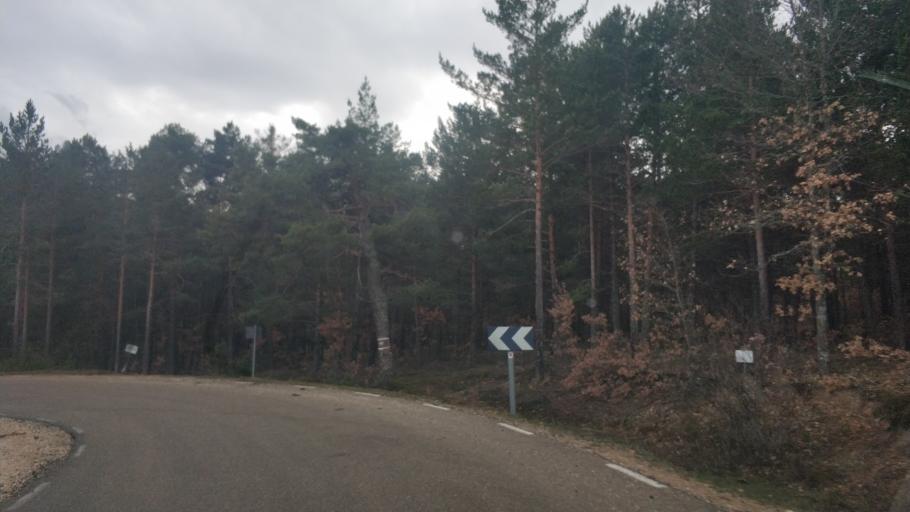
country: ES
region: Castille and Leon
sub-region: Provincia de Burgos
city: Canicosa de la Sierra
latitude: 41.9189
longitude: -3.0392
